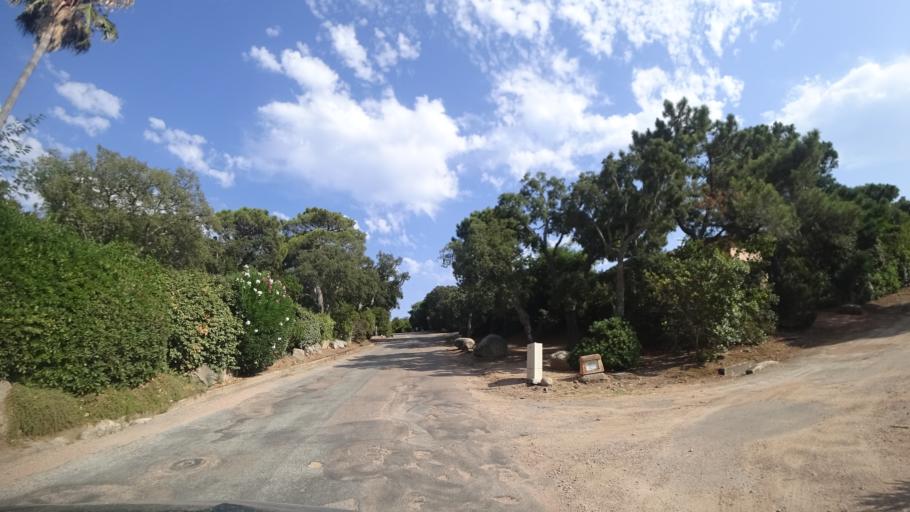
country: FR
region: Corsica
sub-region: Departement de la Corse-du-Sud
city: Porto-Vecchio
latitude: 41.6206
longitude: 9.3456
